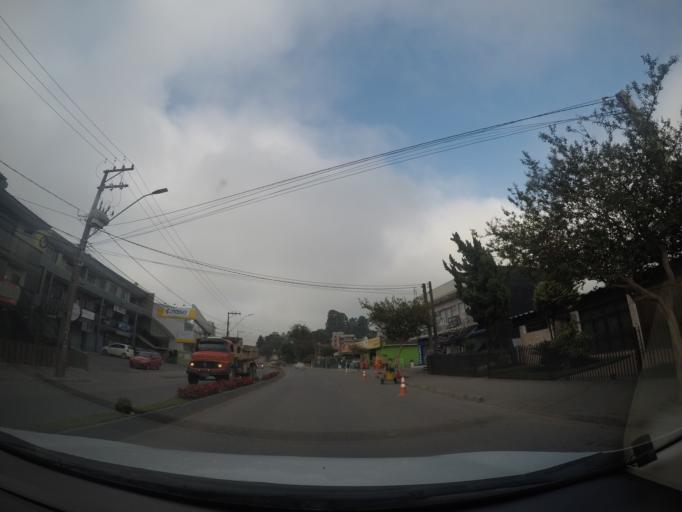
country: BR
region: Parana
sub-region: Colombo
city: Colombo
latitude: -25.2939
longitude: -49.2236
